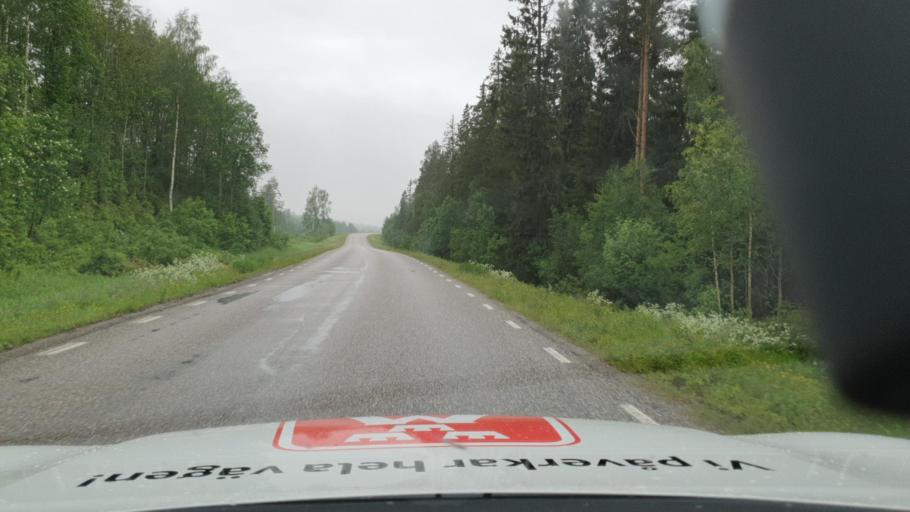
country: SE
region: Vaesterbotten
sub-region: Vannas Kommun
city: Vaennaes
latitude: 63.7731
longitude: 19.6112
